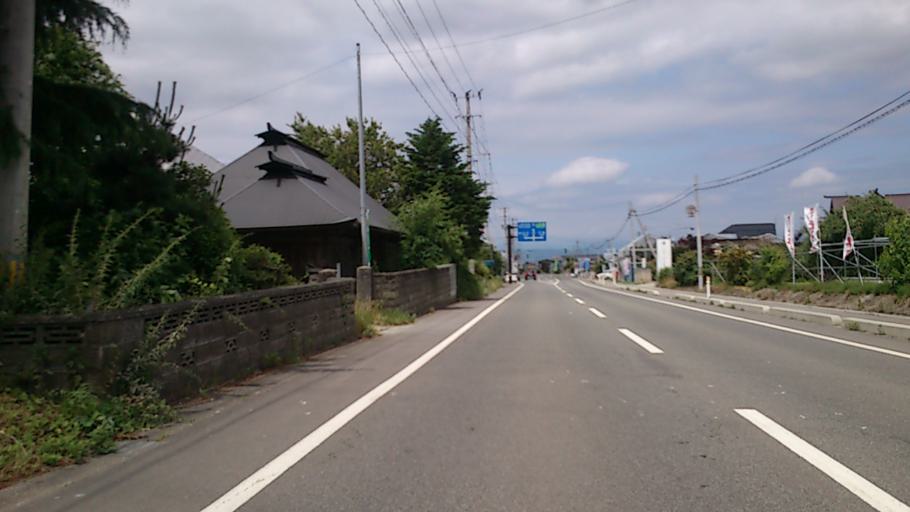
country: JP
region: Yamagata
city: Tendo
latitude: 38.3129
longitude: 140.4128
